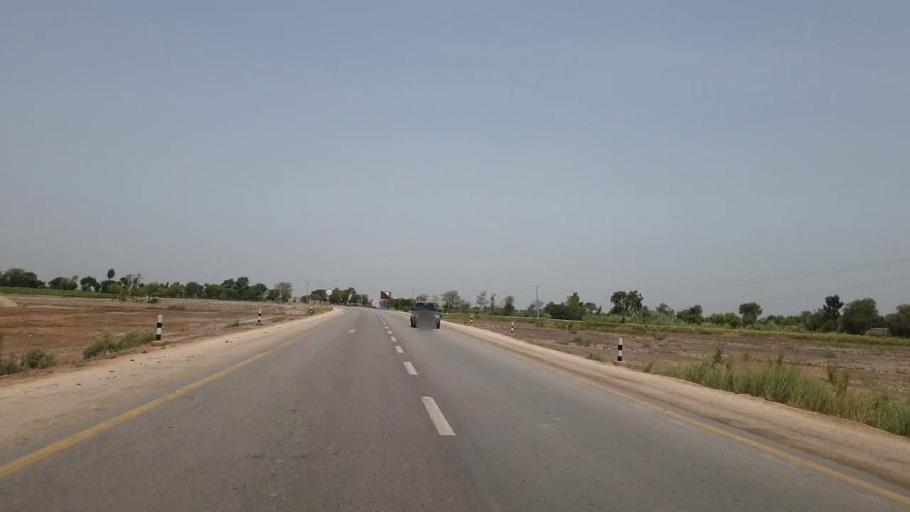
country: PK
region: Sindh
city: Shahpur Chakar
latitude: 26.1922
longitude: 68.5759
